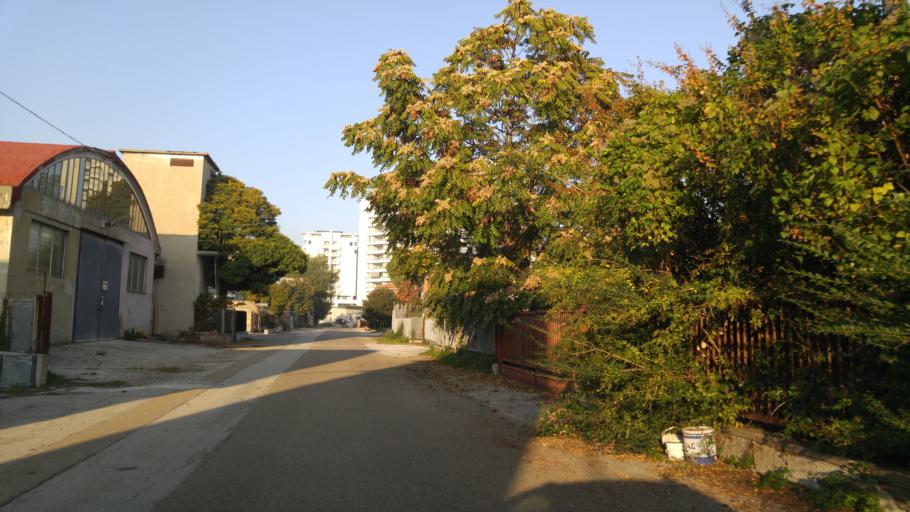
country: IT
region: The Marches
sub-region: Provincia di Pesaro e Urbino
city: Pesaro
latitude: 43.9027
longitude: 12.8882
